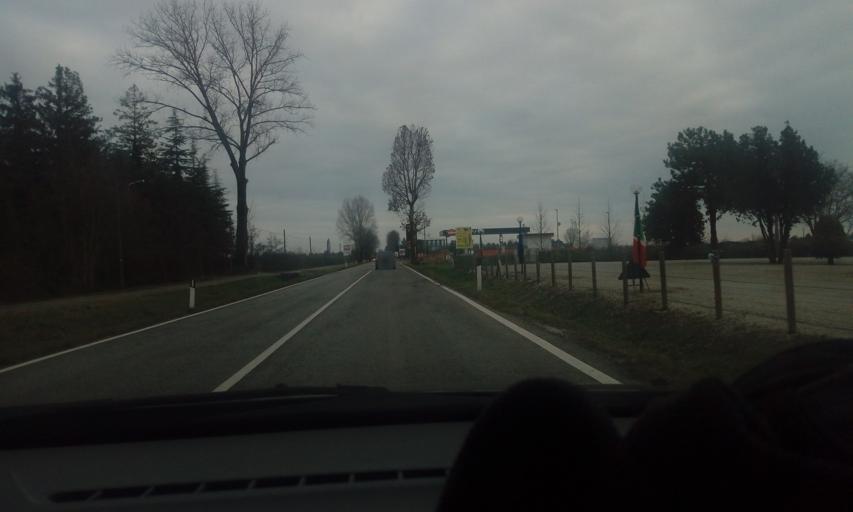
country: IT
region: Friuli Venezia Giulia
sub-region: Provincia di Udine
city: Aquileia
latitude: 45.7870
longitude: 13.3583
